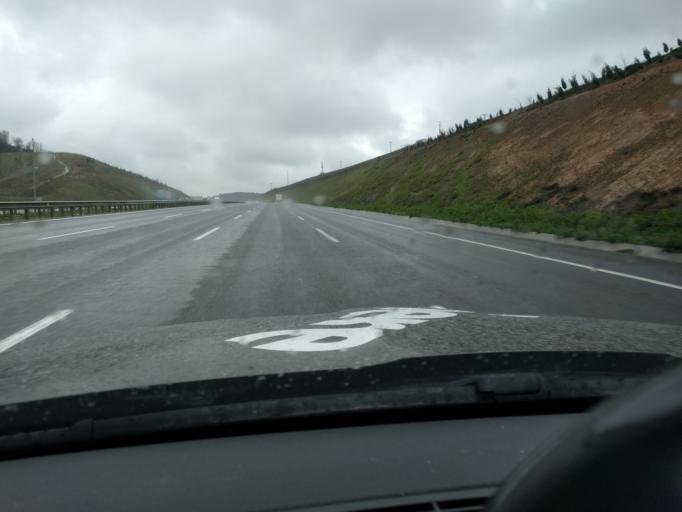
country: TR
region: Istanbul
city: Basaksehir
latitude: 41.1785
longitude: 28.8136
